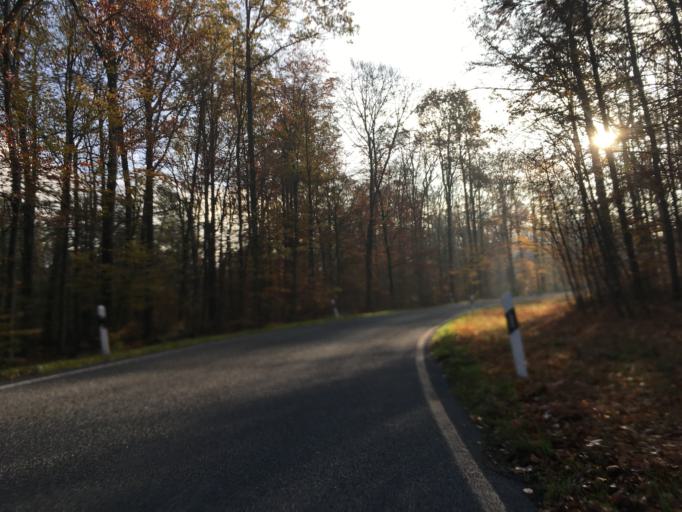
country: DE
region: Brandenburg
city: Schlepzig
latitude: 52.0342
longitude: 13.8628
